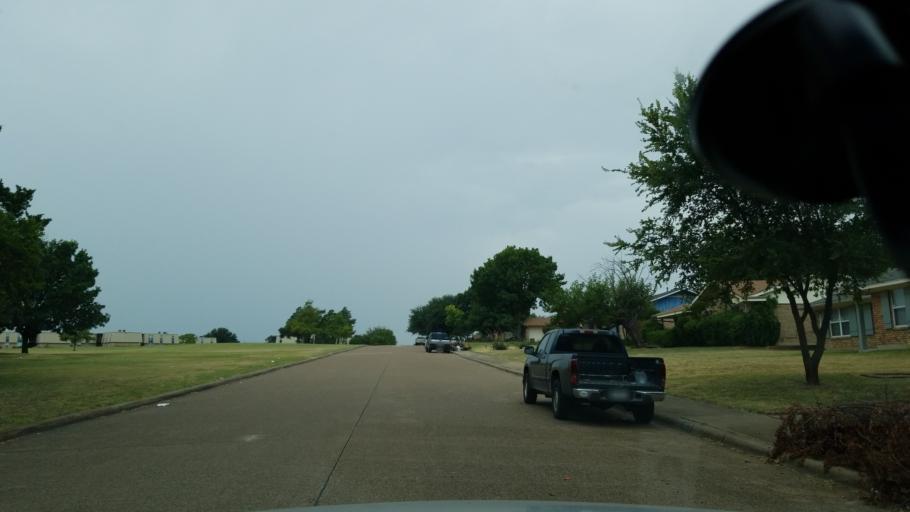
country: US
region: Texas
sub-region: Dallas County
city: Cockrell Hill
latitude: 32.6849
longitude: -96.8527
